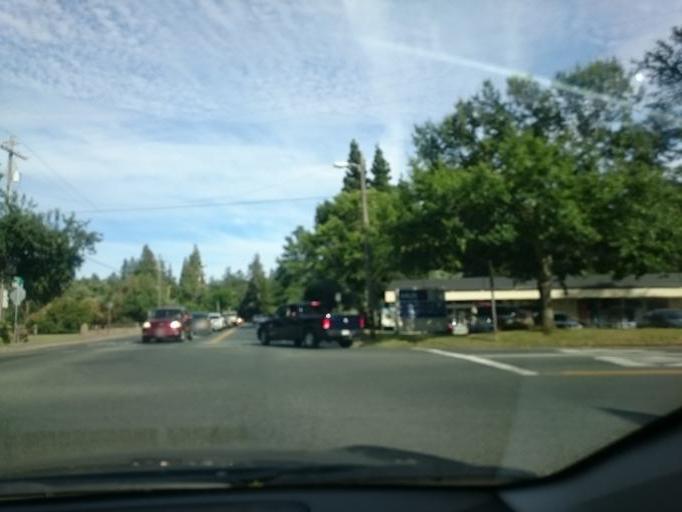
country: US
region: California
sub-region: Napa County
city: Calistoga
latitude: 38.5813
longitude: -122.5964
